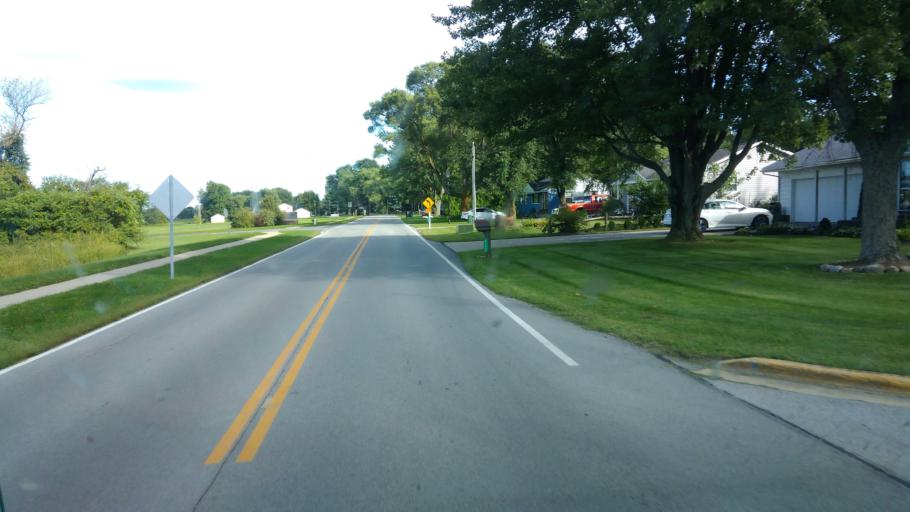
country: US
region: Ohio
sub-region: Sandusky County
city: Clyde
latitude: 41.2867
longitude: -82.9724
